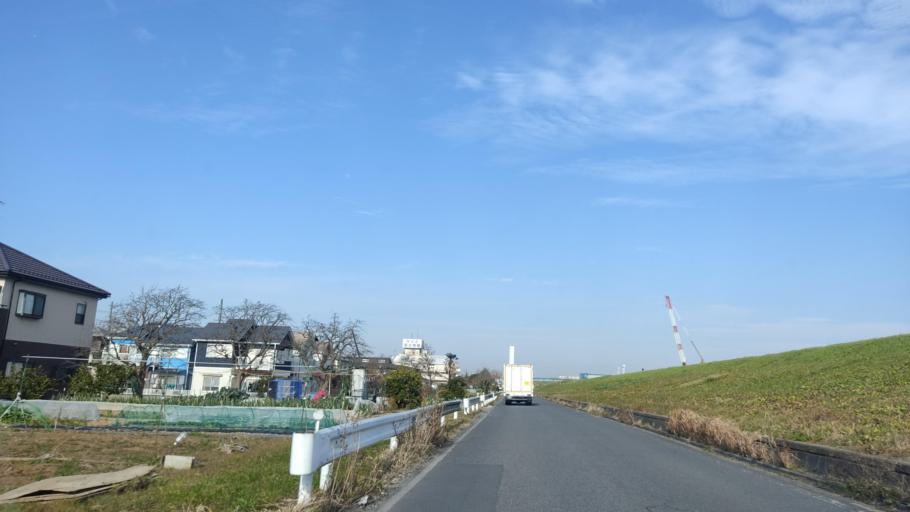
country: JP
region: Chiba
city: Nagareyama
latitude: 35.8596
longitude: 139.8936
